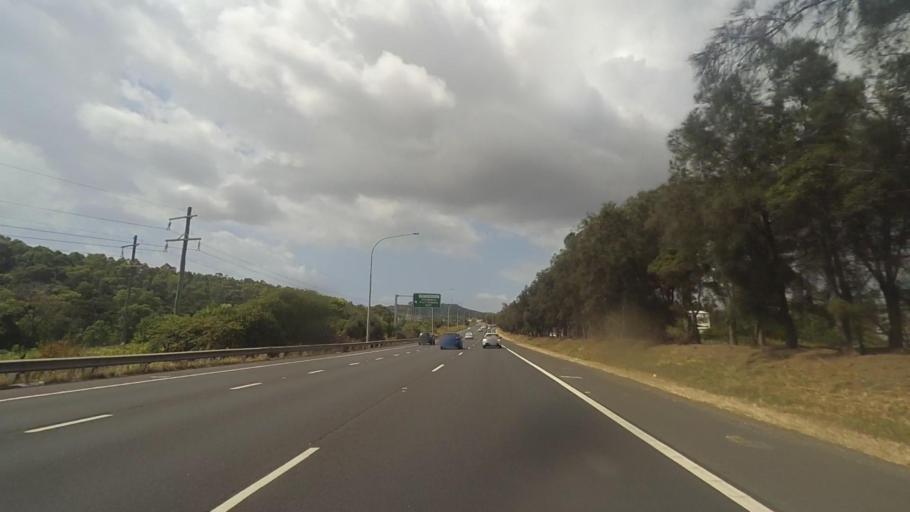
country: AU
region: New South Wales
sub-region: Wollongong
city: Mount Saint Thomas
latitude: -34.4486
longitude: 150.8602
